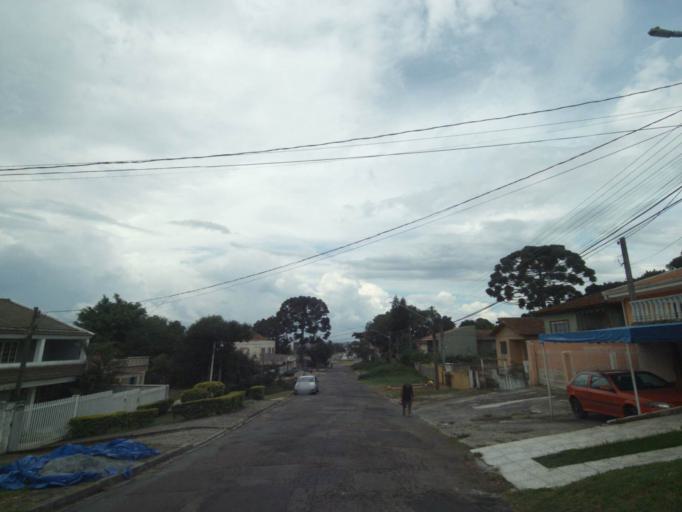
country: BR
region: Parana
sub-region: Pinhais
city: Pinhais
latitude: -25.4434
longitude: -49.2310
